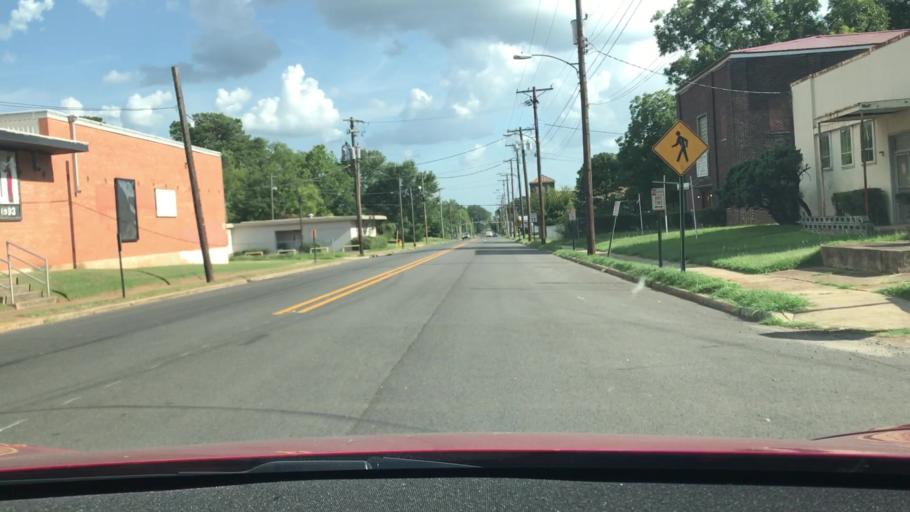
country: US
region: Louisiana
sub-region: Bossier Parish
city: Bossier City
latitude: 32.4452
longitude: -93.7545
